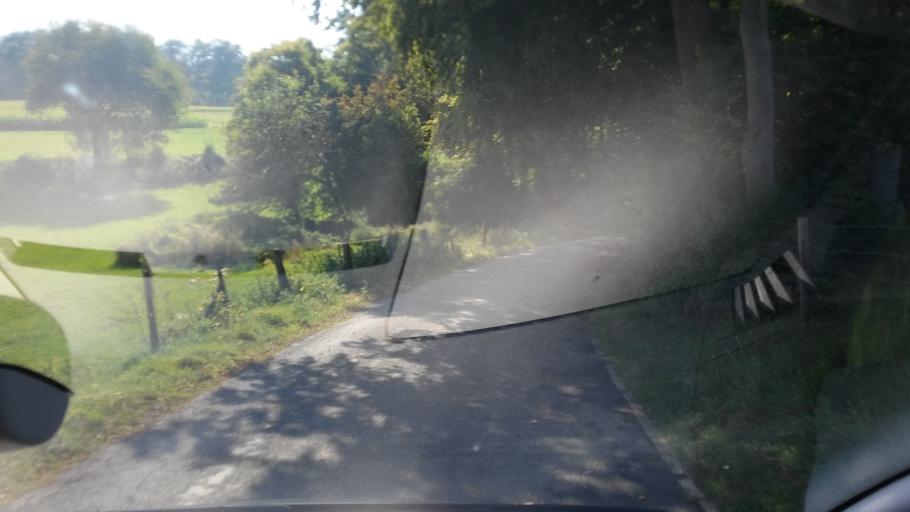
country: LU
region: Luxembourg
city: Eischen
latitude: 49.7085
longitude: 5.8665
